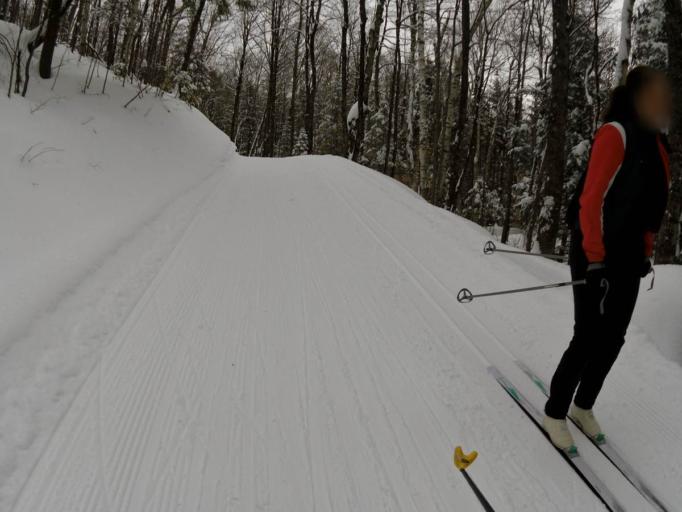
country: CA
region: Quebec
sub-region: Outaouais
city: Wakefield
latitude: 45.5946
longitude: -76.0118
